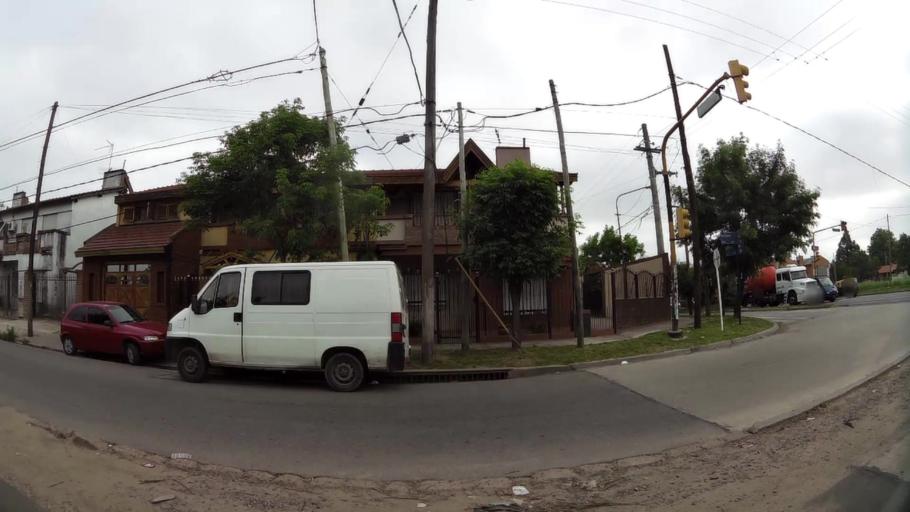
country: AR
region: Buenos Aires
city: San Justo
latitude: -34.7157
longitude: -58.5347
